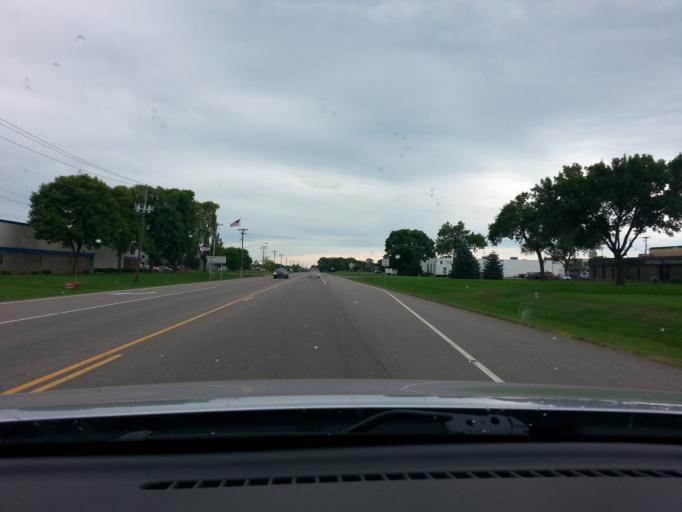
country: US
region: Minnesota
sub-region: Dakota County
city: Lakeville
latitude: 44.6380
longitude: -93.2271
